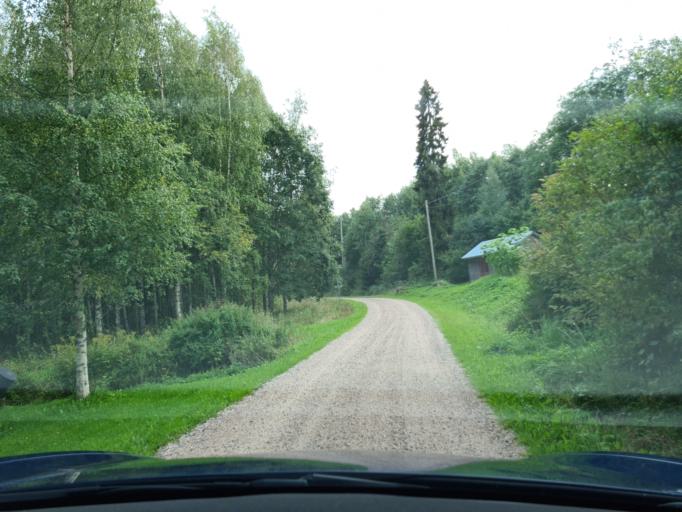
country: FI
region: Uusimaa
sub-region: Helsinki
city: Vihti
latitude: 60.4115
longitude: 24.4935
